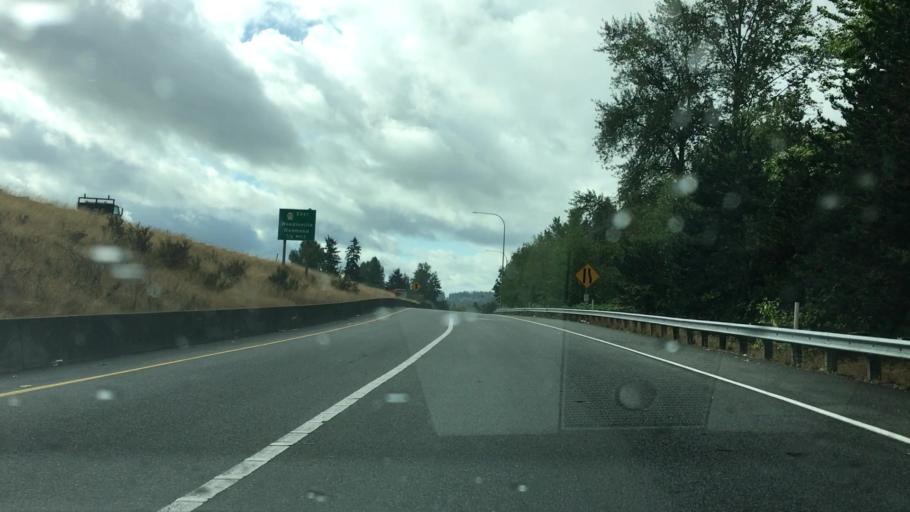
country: US
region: Washington
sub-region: King County
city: Woodinville
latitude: 47.7684
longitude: -122.1568
